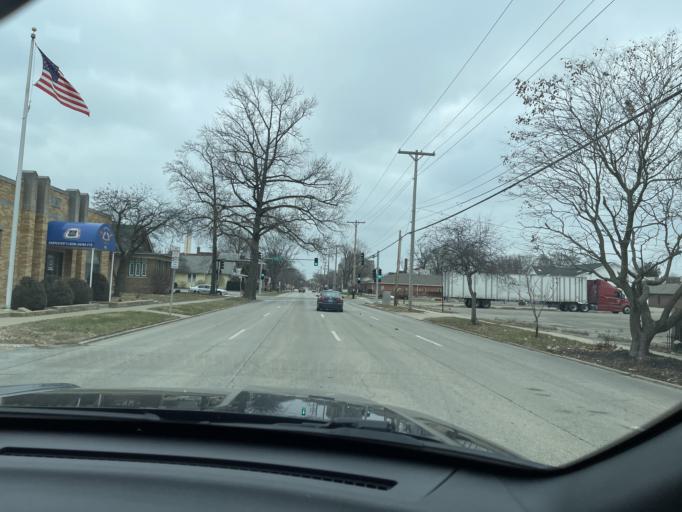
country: US
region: Illinois
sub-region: Sangamon County
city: Springfield
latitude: 39.7940
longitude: -89.6569
